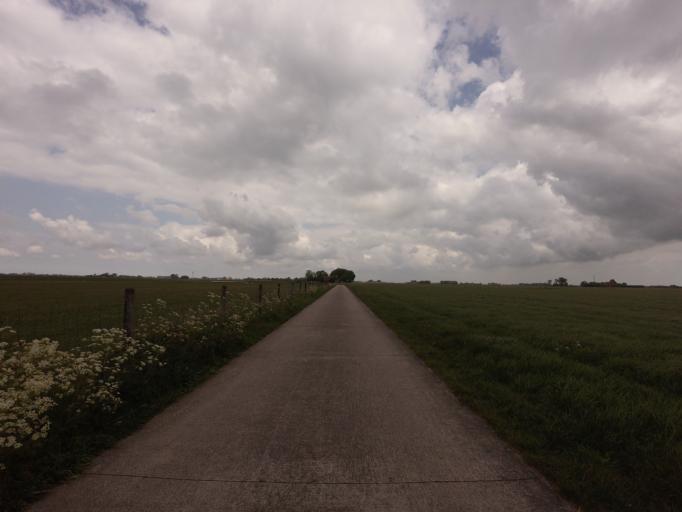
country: NL
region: Friesland
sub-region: Gemeente Littenseradiel
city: Wommels
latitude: 53.1094
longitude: 5.5987
